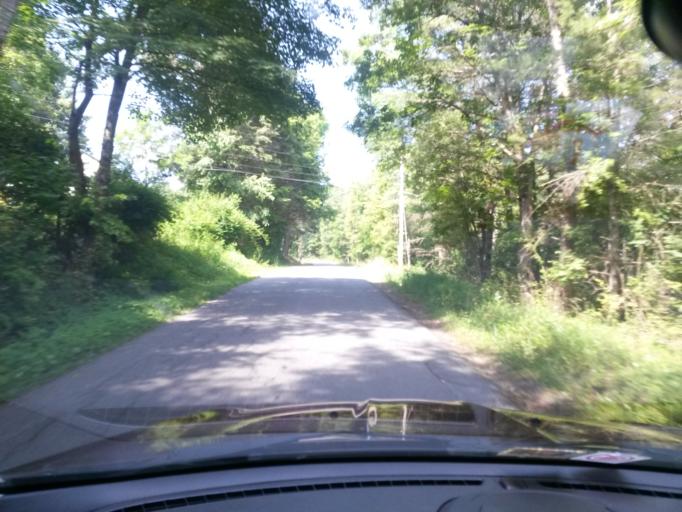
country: US
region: West Virginia
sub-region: Mercer County
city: Princeton
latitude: 37.3986
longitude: -81.1088
